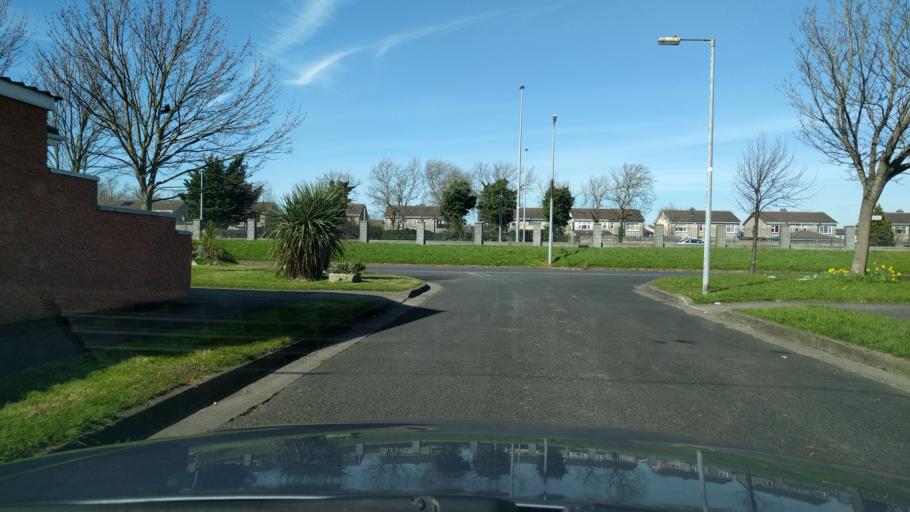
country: IE
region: Leinster
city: Tallaght
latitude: 53.2818
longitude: -6.3861
